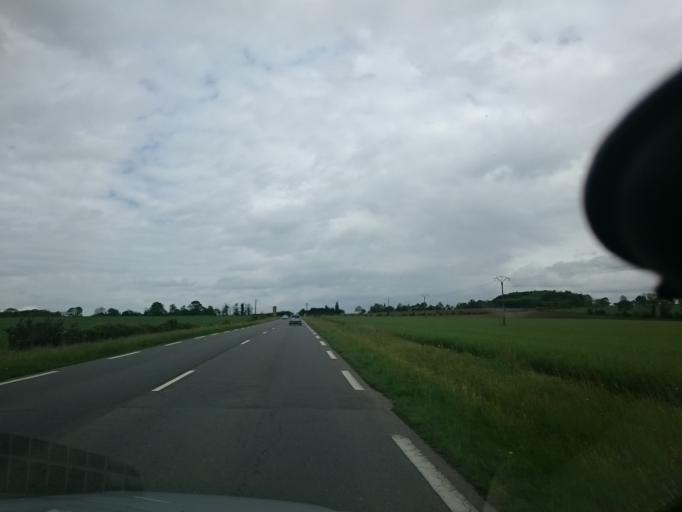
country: FR
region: Brittany
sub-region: Departement d'Ille-et-Vilaine
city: Tremblay
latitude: 48.4238
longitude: -1.4349
